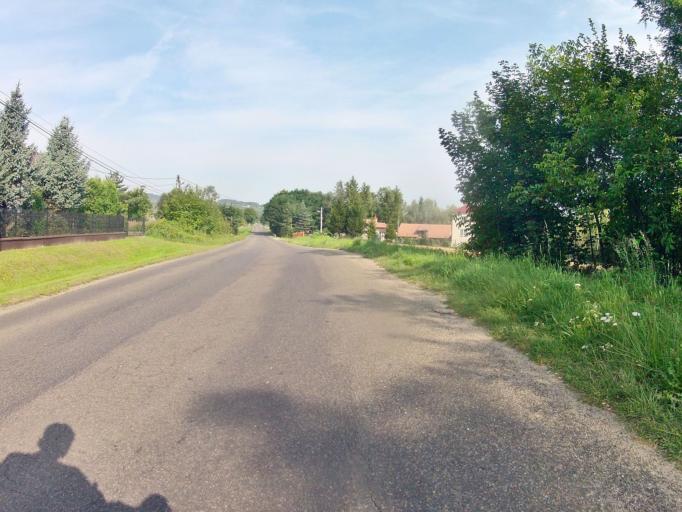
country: PL
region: Subcarpathian Voivodeship
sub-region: Powiat jasielski
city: Kolaczyce
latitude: 49.7854
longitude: 21.4034
